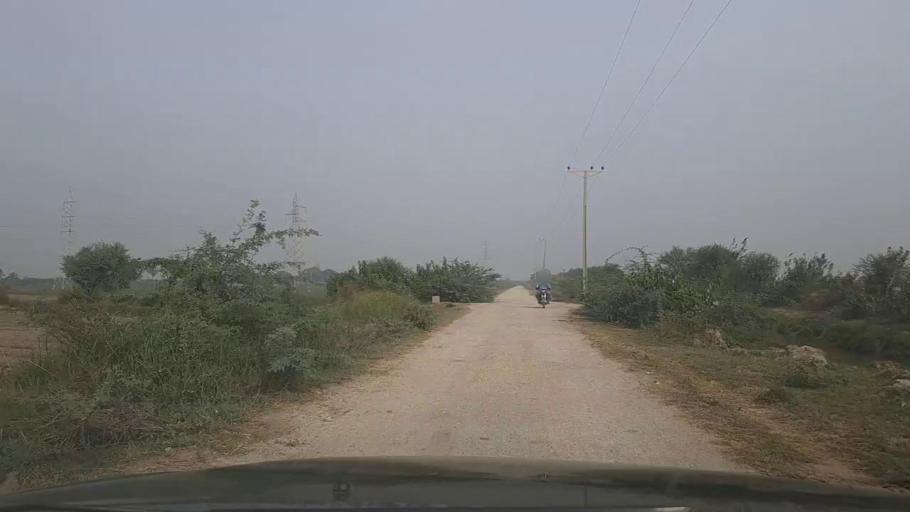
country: PK
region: Sindh
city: Mirpur Sakro
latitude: 24.5699
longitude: 67.7895
